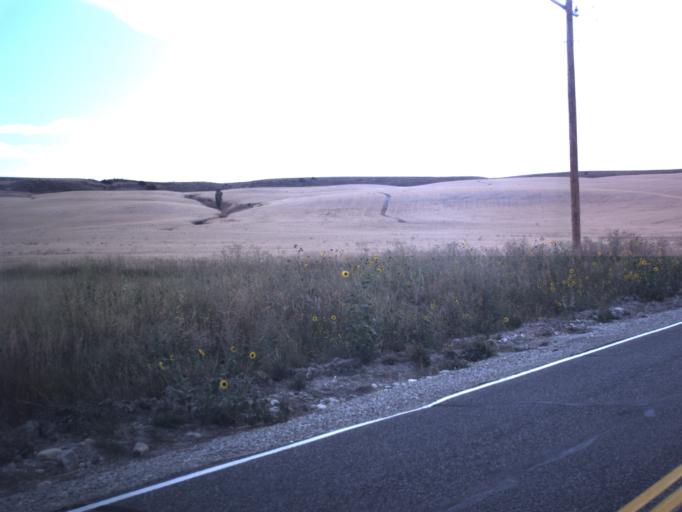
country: US
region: Utah
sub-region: Cache County
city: Lewiston
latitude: 41.9176
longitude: -111.9622
